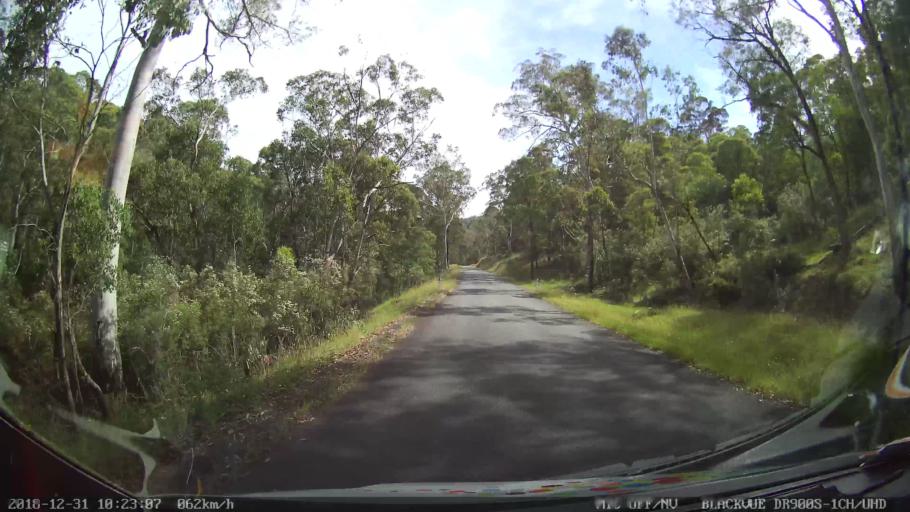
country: AU
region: New South Wales
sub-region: Snowy River
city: Jindabyne
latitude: -36.5196
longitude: 148.1434
